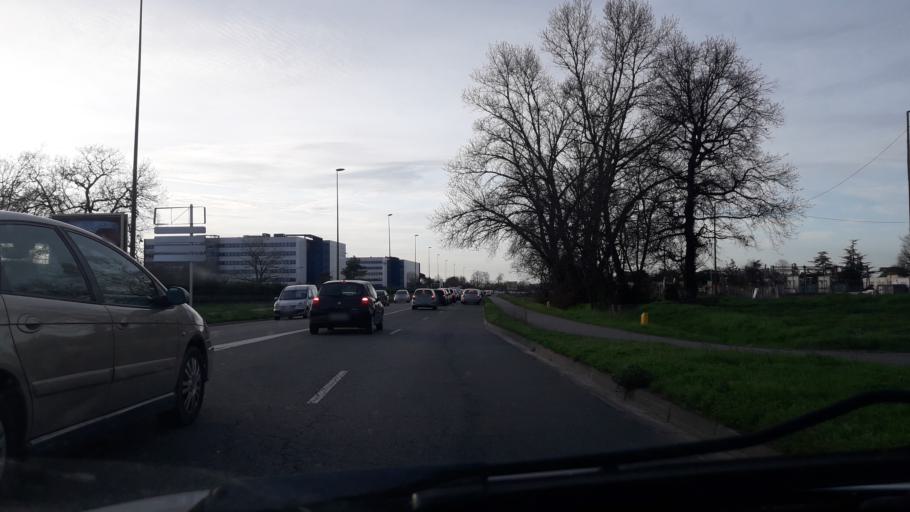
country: FR
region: Midi-Pyrenees
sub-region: Departement de la Haute-Garonne
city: Cugnaux
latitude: 43.5654
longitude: 1.3826
